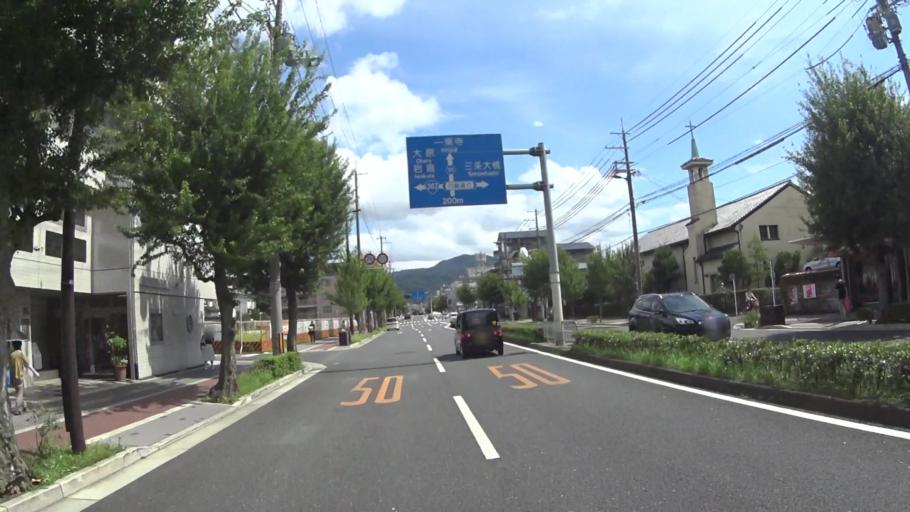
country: JP
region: Kyoto
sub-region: Kyoto-shi
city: Kamigyo-ku
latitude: 35.0441
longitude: 135.7773
